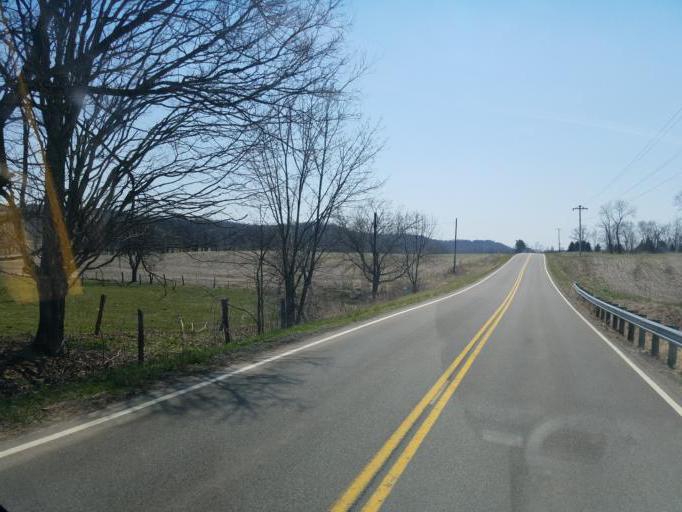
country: US
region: Ohio
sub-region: Ashland County
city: Loudonville
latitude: 40.7174
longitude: -82.2873
